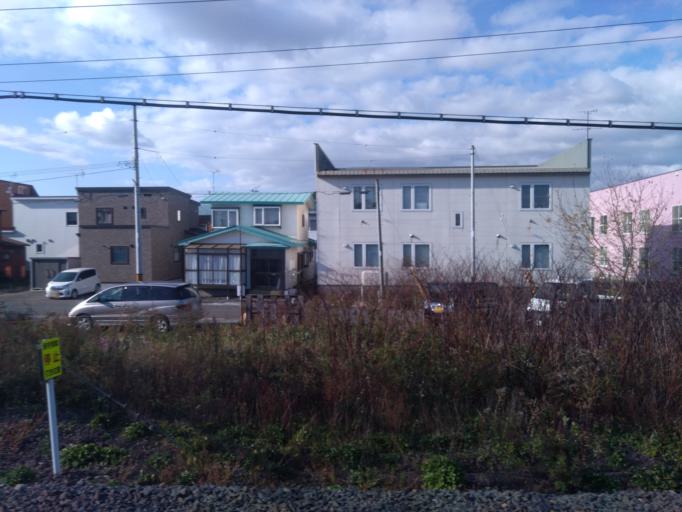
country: JP
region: Hokkaido
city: Muroran
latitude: 42.3546
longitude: 141.0331
